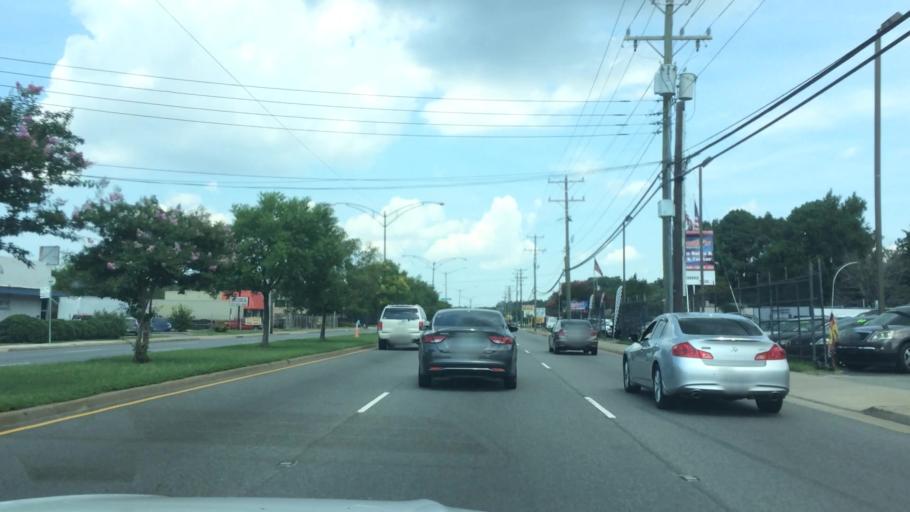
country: US
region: Virginia
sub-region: City of Newport News
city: Newport News
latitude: 37.0333
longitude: -76.4531
